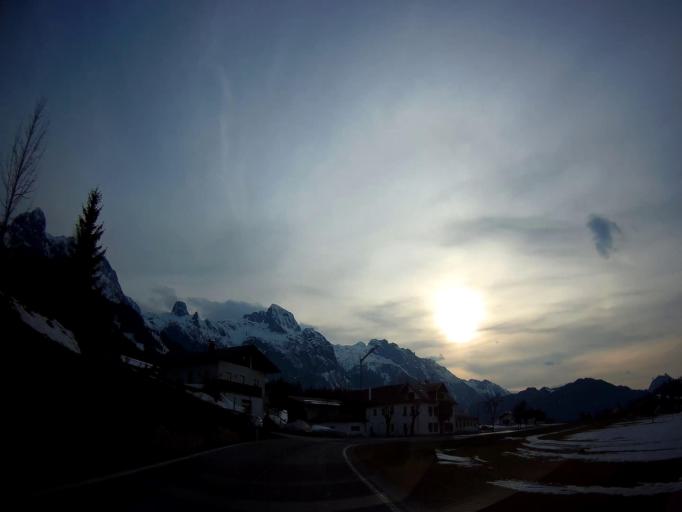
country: AT
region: Salzburg
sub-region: Politischer Bezirk Hallein
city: Abtenau
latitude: 47.5609
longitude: 13.3792
